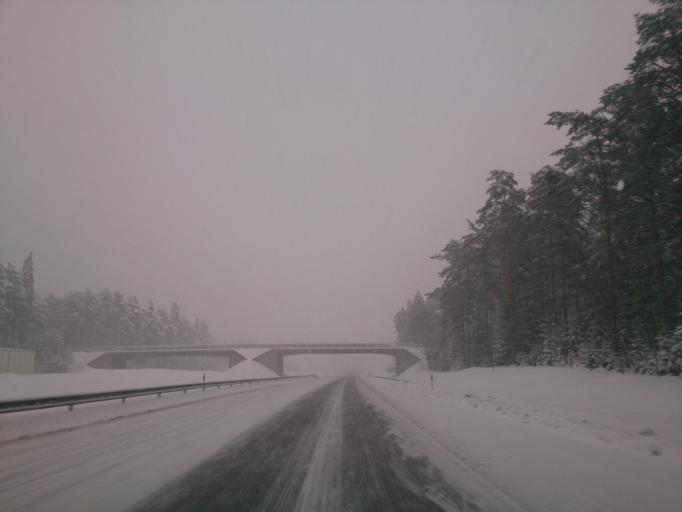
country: SE
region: Soedermanland
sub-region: Nykopings Kommun
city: Svalsta
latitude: 58.7569
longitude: 16.8559
